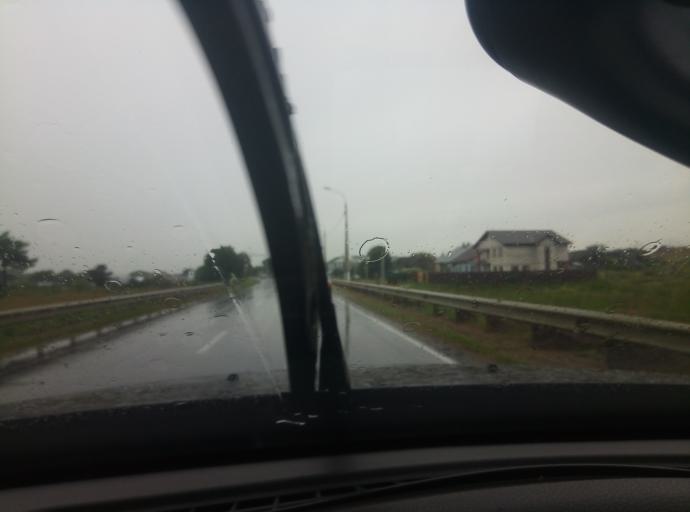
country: RU
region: Kaluga
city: Kremenki
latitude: 54.8789
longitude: 37.1355
